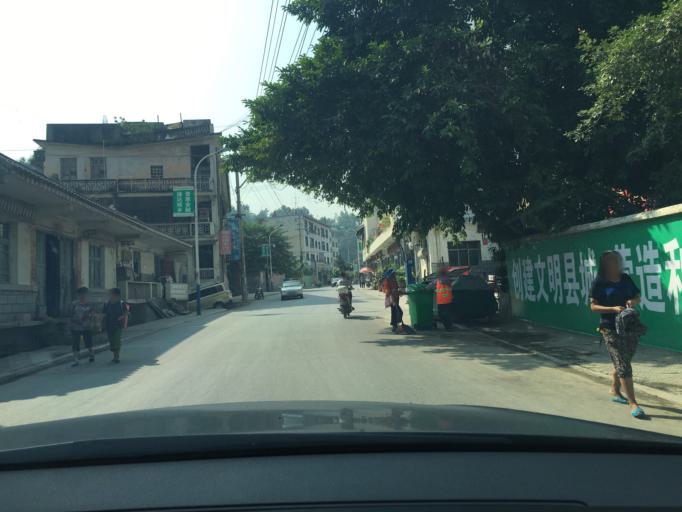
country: CN
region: Guangxi Zhuangzu Zizhiqu
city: Xinzhou
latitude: 24.9875
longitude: 105.8018
